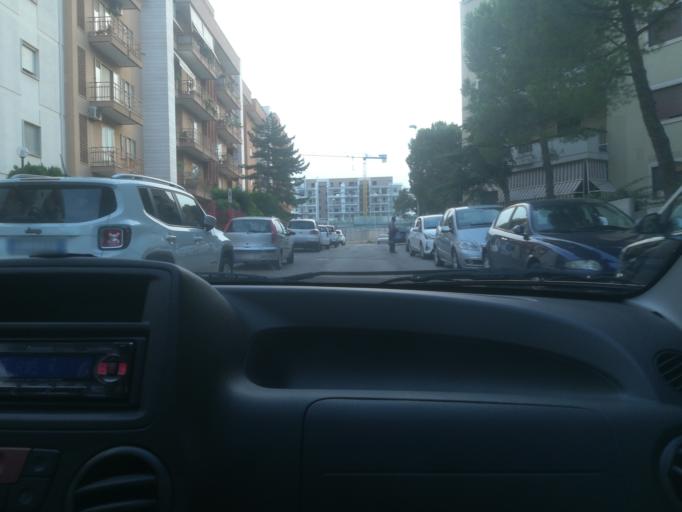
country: IT
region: Apulia
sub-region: Provincia di Bari
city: Monopoli
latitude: 40.9470
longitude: 17.3033
